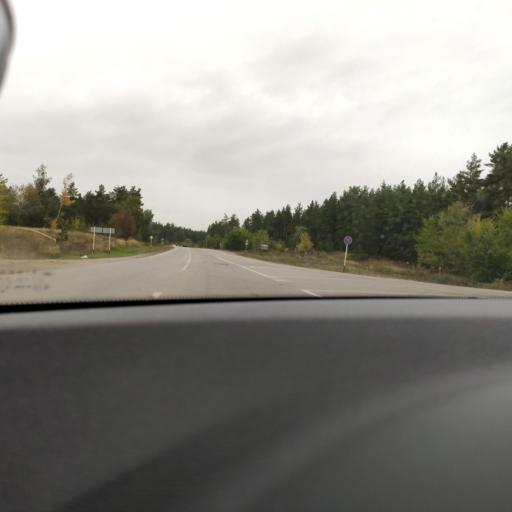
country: RU
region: Samara
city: Mirnyy
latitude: 53.5379
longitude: 50.3004
